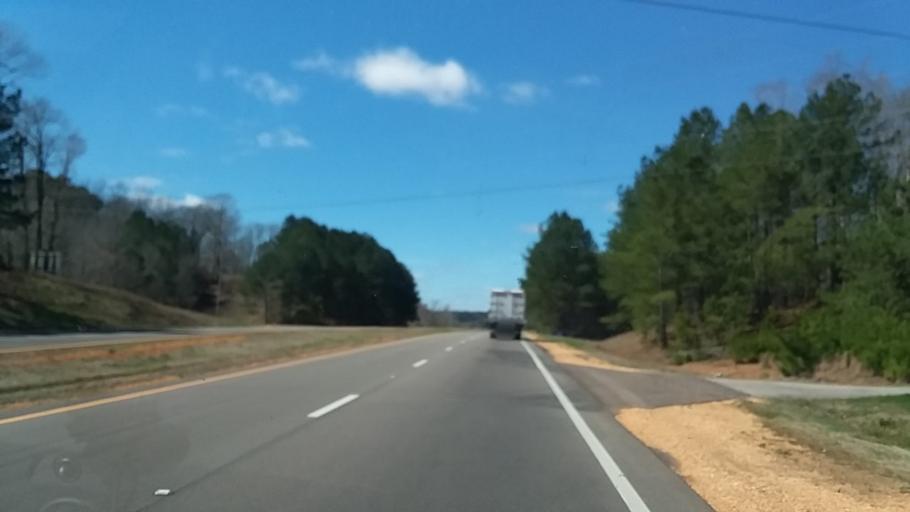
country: US
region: Mississippi
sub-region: Tishomingo County
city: Iuka
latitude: 34.8444
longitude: -88.3296
